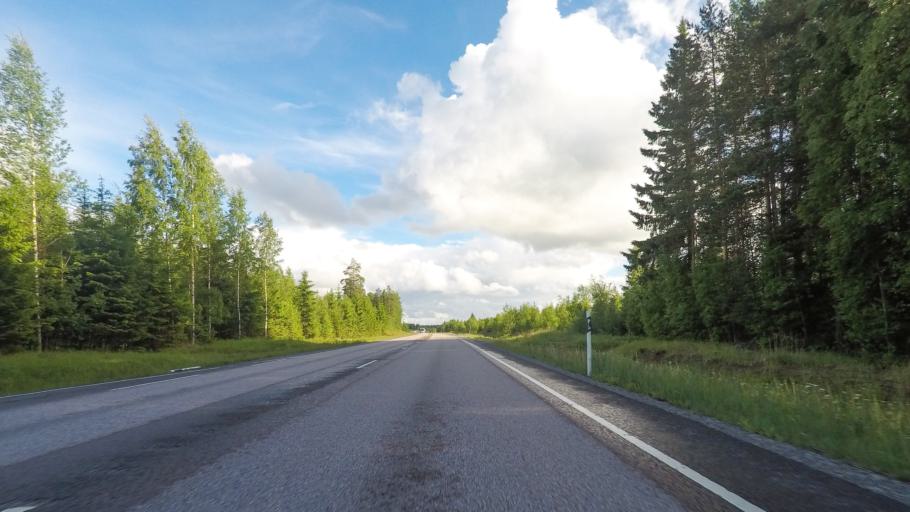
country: FI
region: Paijanne Tavastia
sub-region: Lahti
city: Hartola
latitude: 61.5959
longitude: 26.0079
